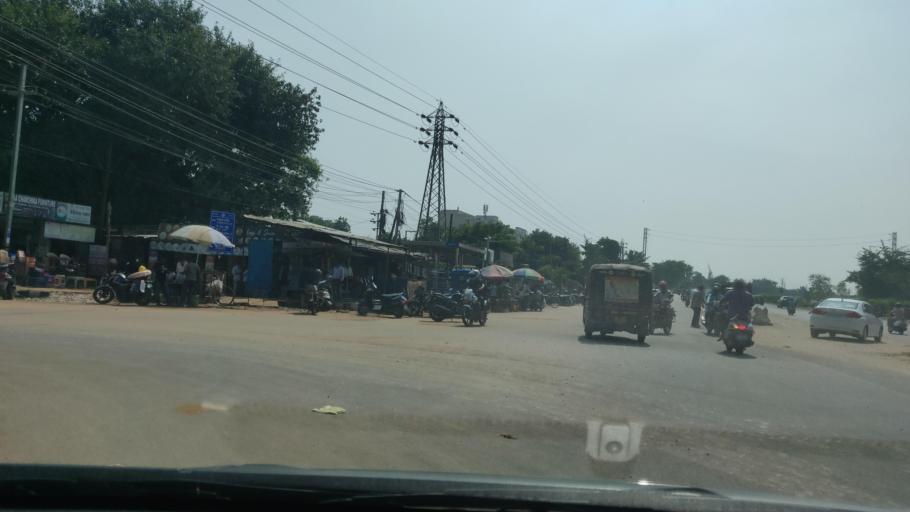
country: IN
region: Odisha
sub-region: Khordha
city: Bhubaneshwar
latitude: 20.2492
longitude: 85.7838
